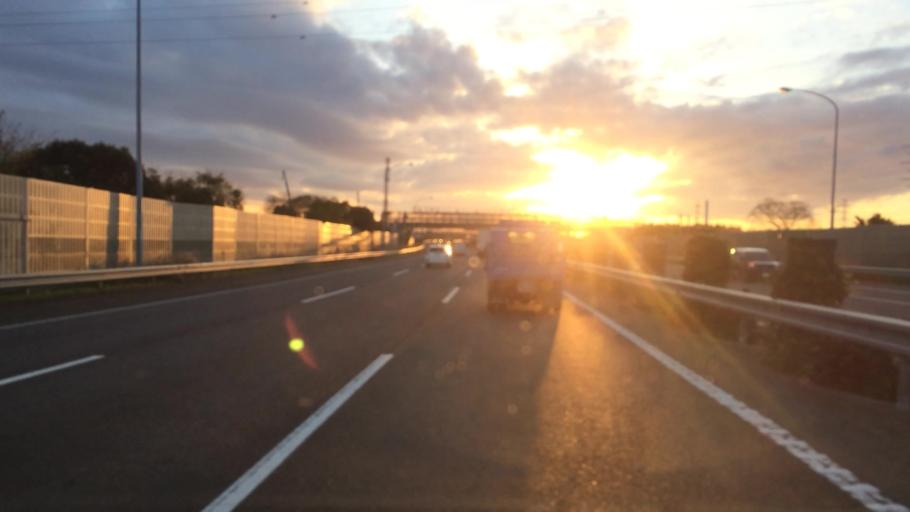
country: JP
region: Chiba
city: Yotsukaido
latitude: 35.6784
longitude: 140.1375
